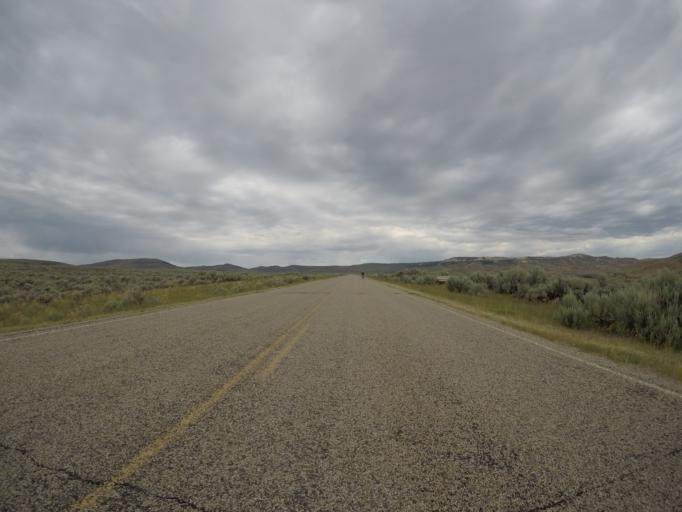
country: US
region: Wyoming
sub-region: Lincoln County
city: Kemmerer
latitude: 41.8303
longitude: -110.7698
